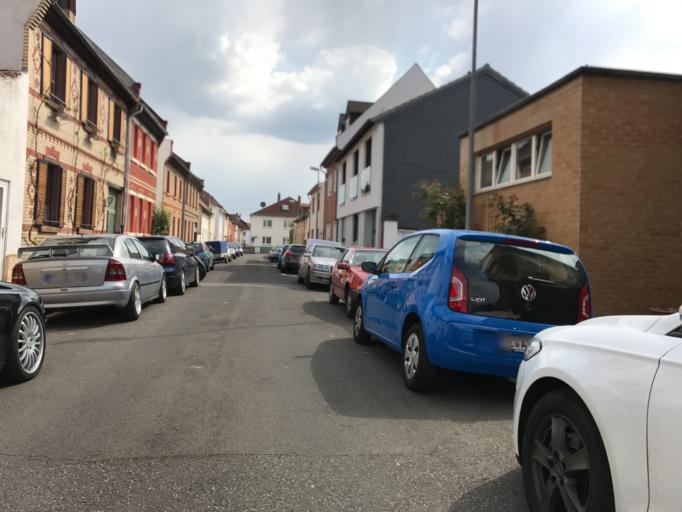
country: DE
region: Rheinland-Pfalz
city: Mainz
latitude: 49.9632
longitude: 8.2786
